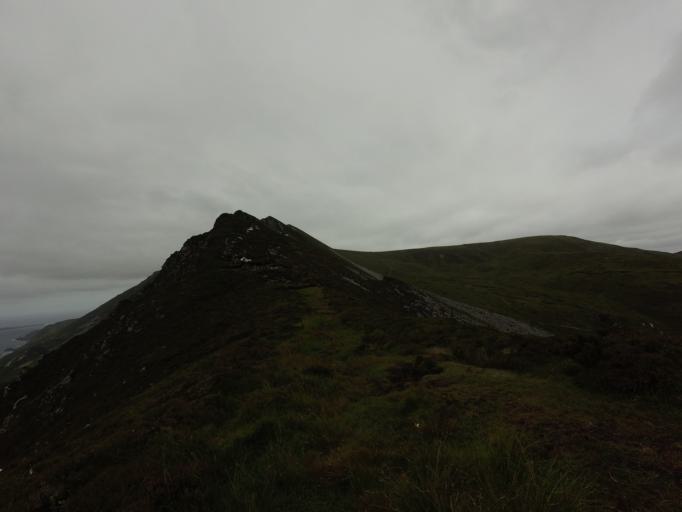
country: IE
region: Ulster
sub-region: County Donegal
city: Killybegs
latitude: 54.6416
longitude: -8.6836
